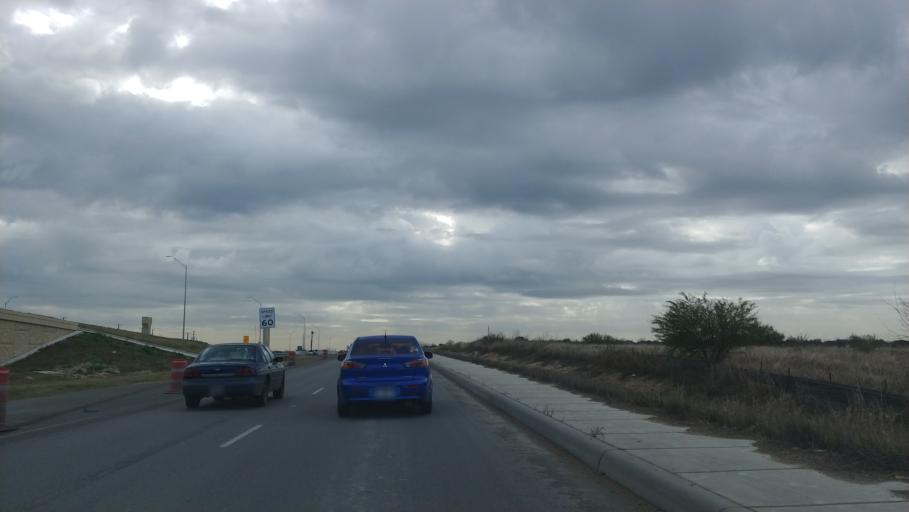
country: US
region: Texas
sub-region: Bexar County
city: Lackland Air Force Base
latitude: 29.4023
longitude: -98.7070
